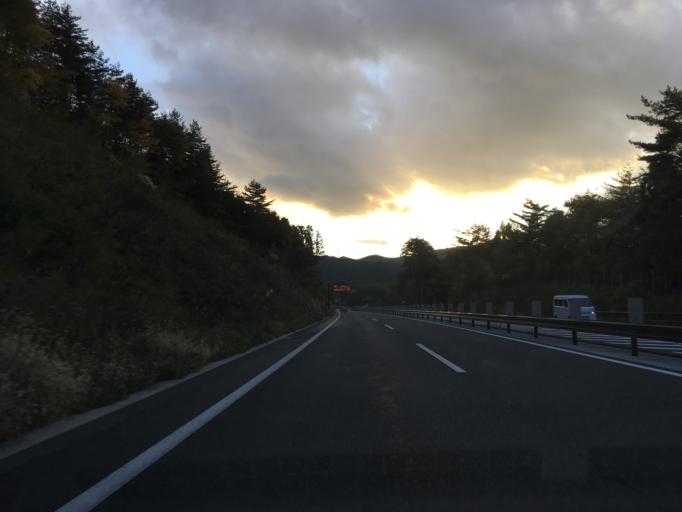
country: JP
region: Iwate
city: Tono
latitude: 39.2976
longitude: 141.4126
